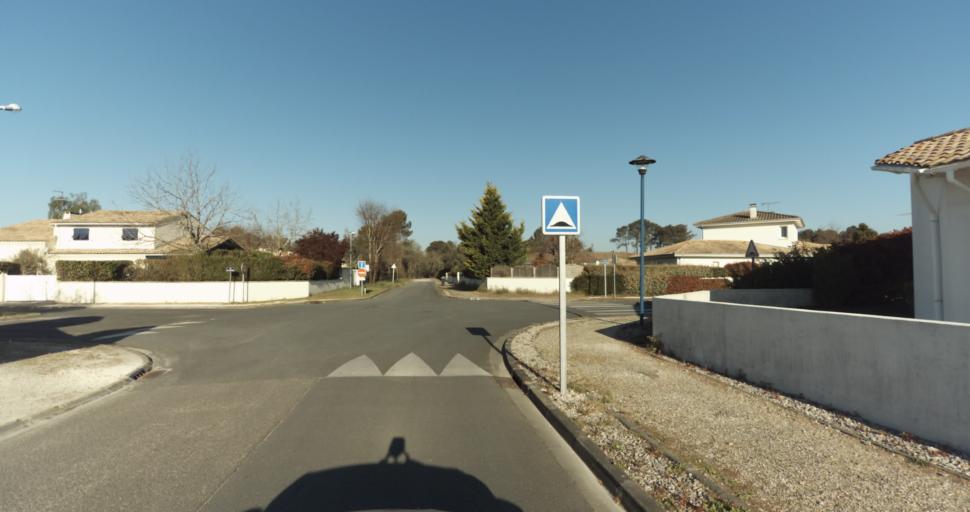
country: FR
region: Aquitaine
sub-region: Departement de la Gironde
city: Martignas-sur-Jalle
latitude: 44.8120
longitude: -0.7967
